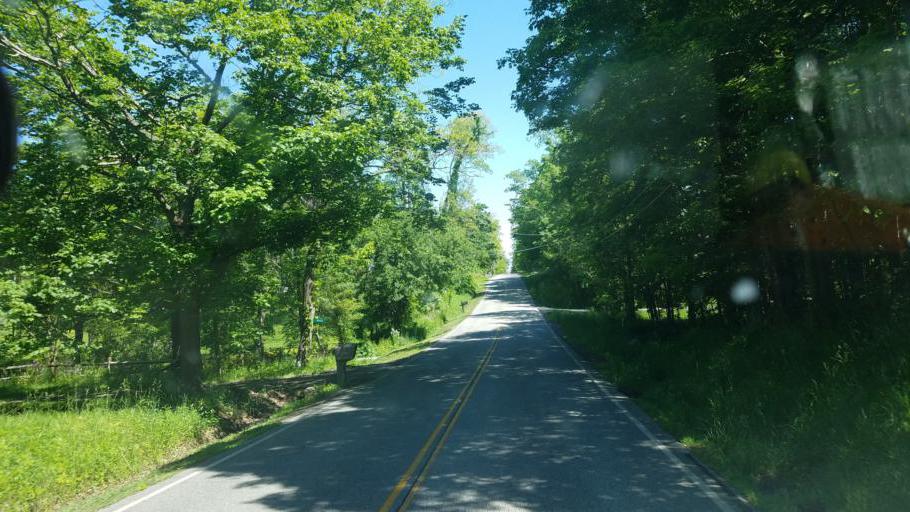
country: US
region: Ohio
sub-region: Geauga County
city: Bainbridge
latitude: 41.3635
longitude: -81.3089
